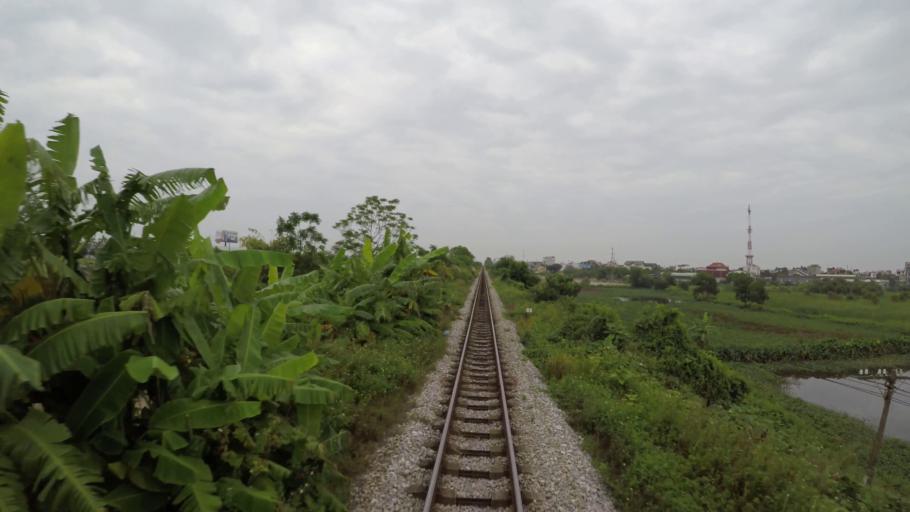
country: VN
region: Hai Duong
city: Thanh Pho Hai Duong
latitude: 20.9460
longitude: 106.3613
